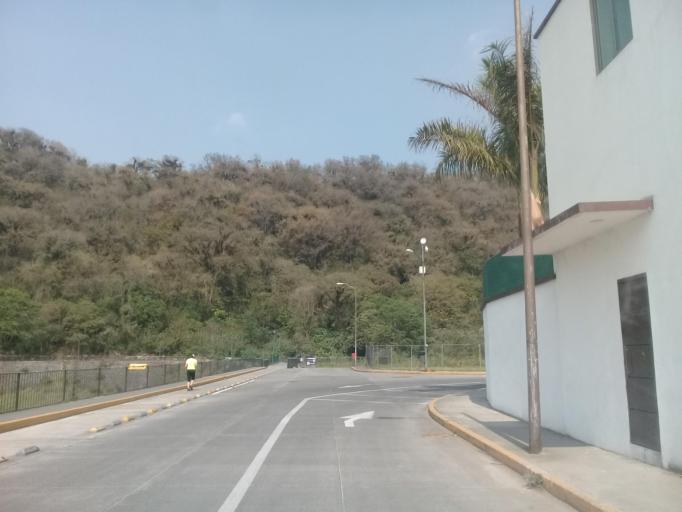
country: MX
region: Veracruz
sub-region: Mariano Escobedo
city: Palmira
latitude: 18.8793
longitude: -97.1033
